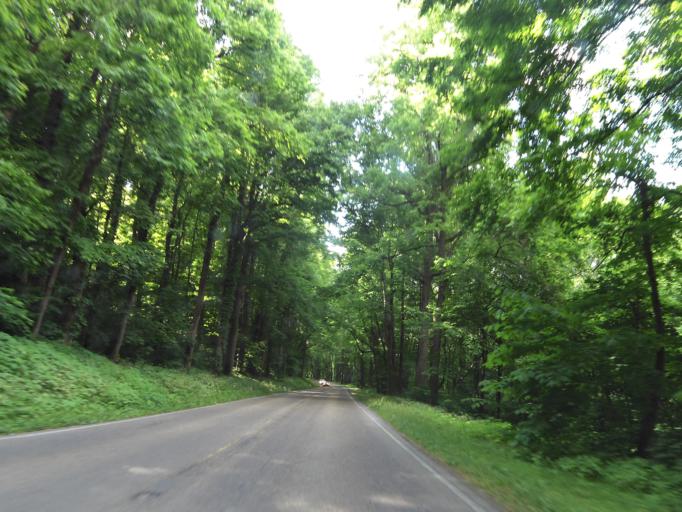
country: US
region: Tennessee
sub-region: Sevier County
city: Gatlinburg
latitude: 35.6556
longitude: -83.5176
